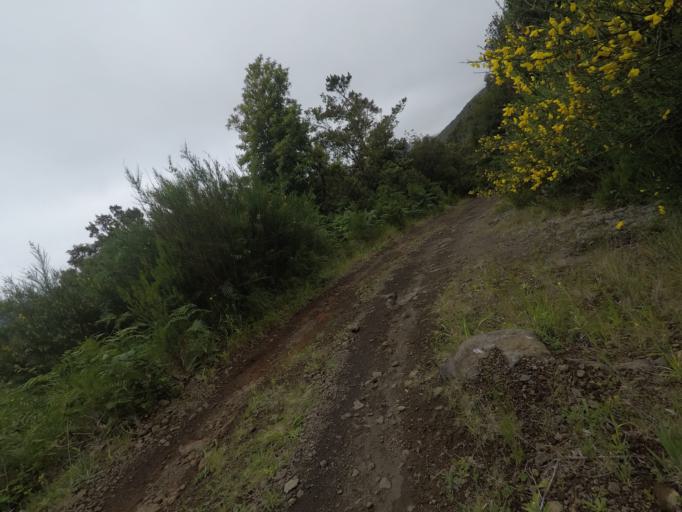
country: PT
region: Madeira
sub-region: Sao Vicente
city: Sao Vicente
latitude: 32.7729
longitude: -17.0534
